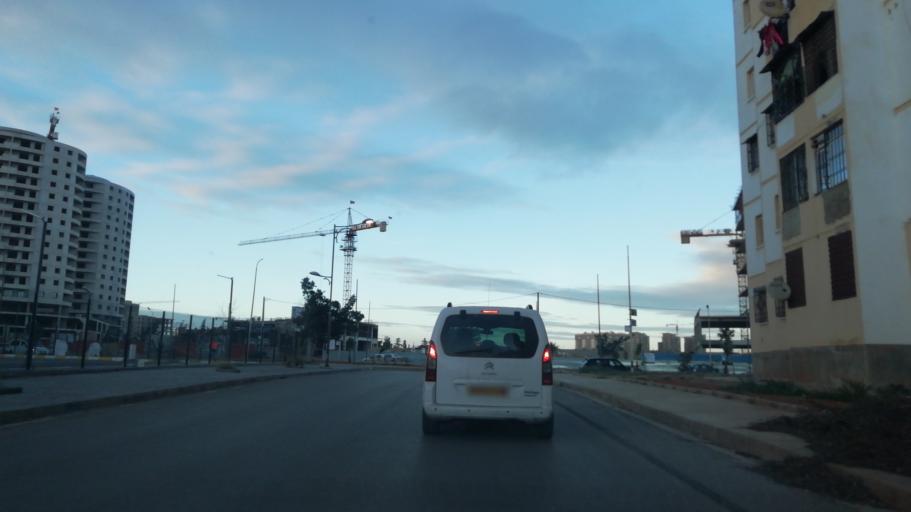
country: DZ
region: Oran
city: Bir el Djir
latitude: 35.7066
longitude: -0.5602
